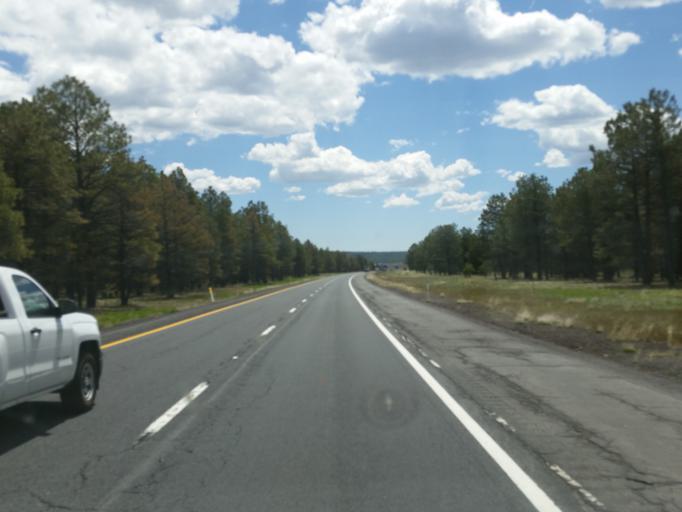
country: US
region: Arizona
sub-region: Coconino County
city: Parks
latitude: 35.2470
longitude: -111.8502
